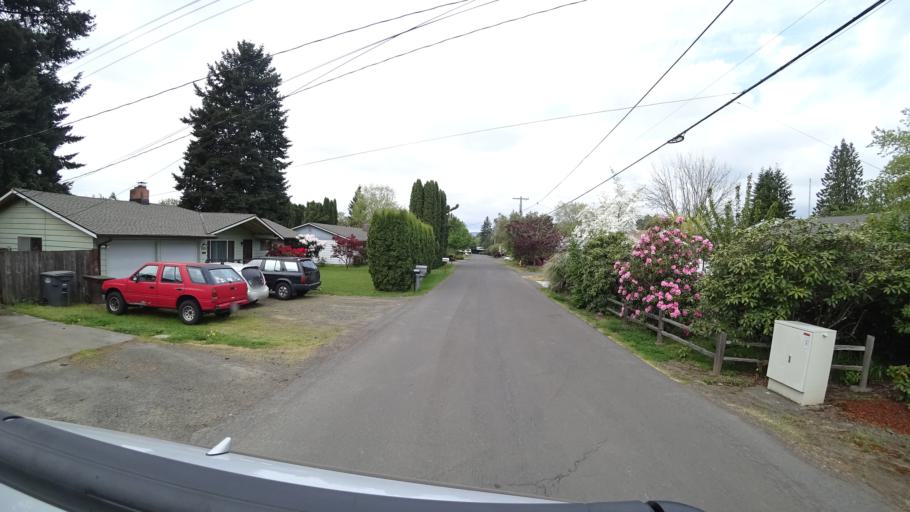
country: US
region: Oregon
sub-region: Washington County
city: Hillsboro
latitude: 45.5281
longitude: -123.0009
